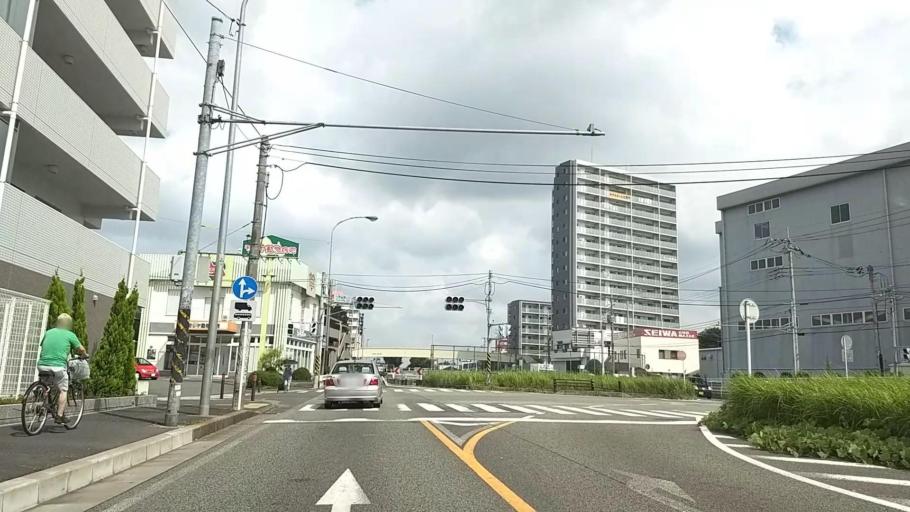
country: JP
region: Tokyo
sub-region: Machida-shi
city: Machida
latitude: 35.5161
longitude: 139.4557
